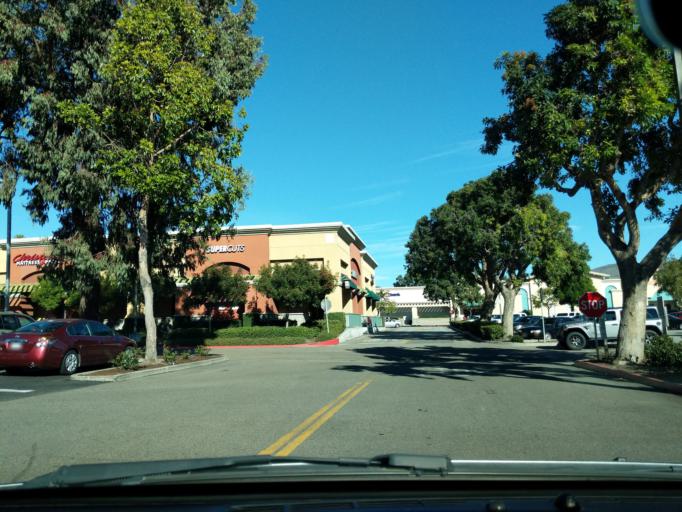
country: US
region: California
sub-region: San Luis Obispo County
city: San Luis Obispo
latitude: 35.2627
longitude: -120.6770
